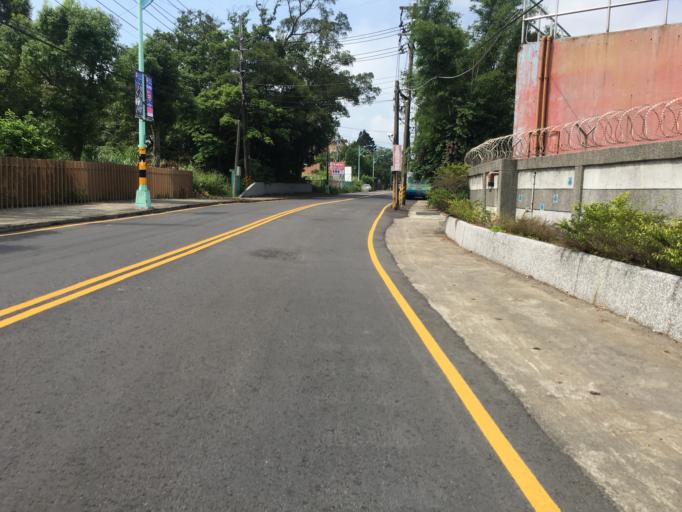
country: TW
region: Taiwan
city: Daxi
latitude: 24.8443
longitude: 121.2417
